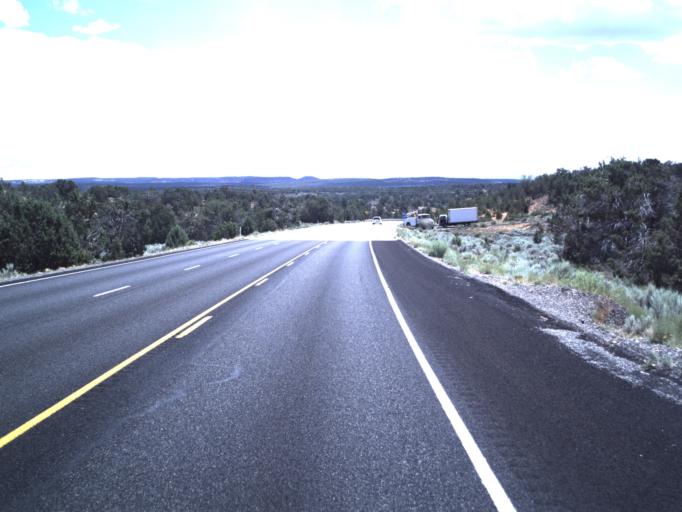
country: US
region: Utah
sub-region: Kane County
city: Kanab
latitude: 37.1519
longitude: -112.5722
